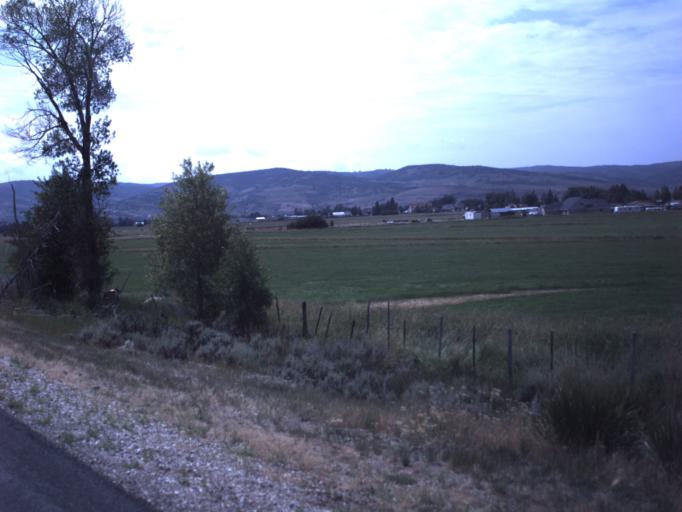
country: US
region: Utah
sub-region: Summit County
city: Francis
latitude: 40.6099
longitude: -111.2584
